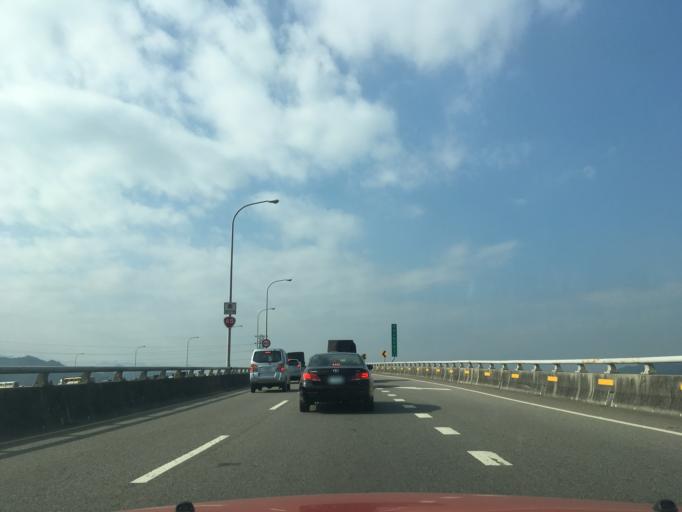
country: TW
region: Taipei
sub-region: Taipei
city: Banqiao
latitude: 24.9742
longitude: 121.4336
